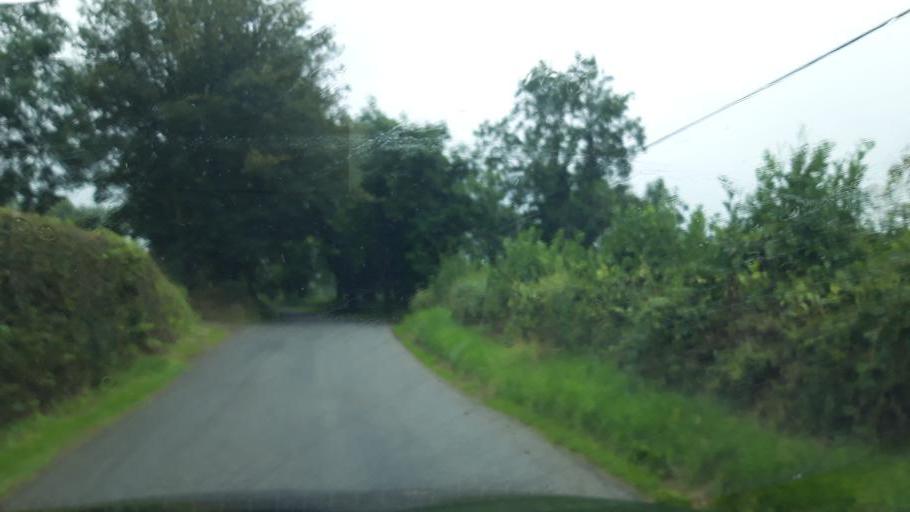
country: IE
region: Leinster
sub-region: Kilkenny
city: Ballyragget
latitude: 52.6848
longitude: -7.4317
